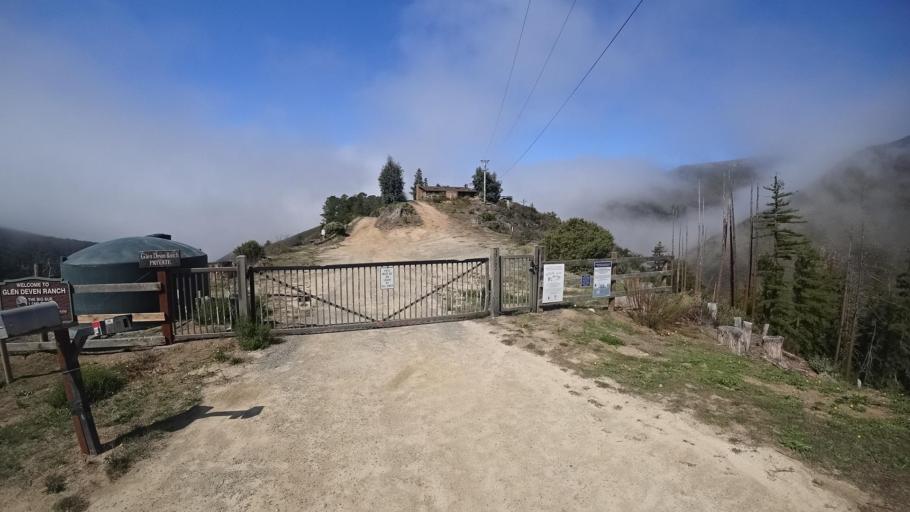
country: US
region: California
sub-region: Monterey County
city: Carmel Valley Village
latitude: 36.3996
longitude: -121.8830
